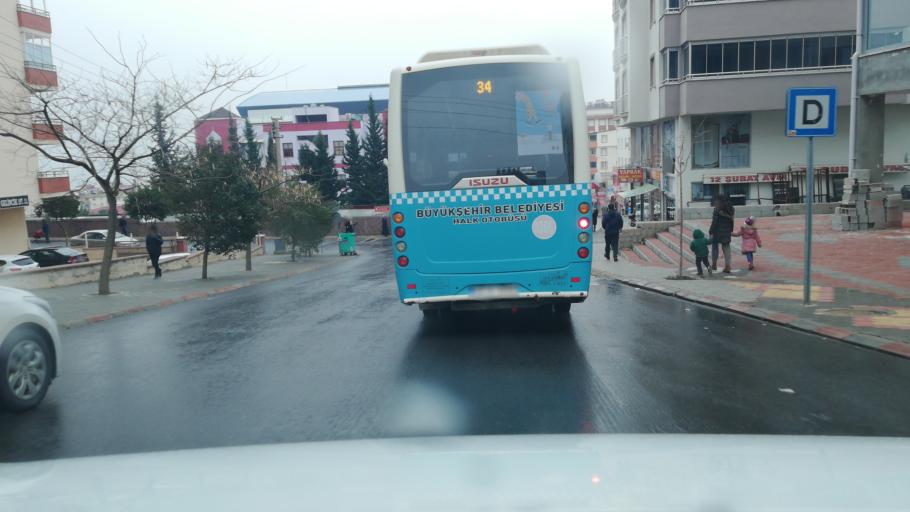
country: TR
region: Kahramanmaras
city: Kahramanmaras
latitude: 37.5952
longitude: 36.8832
